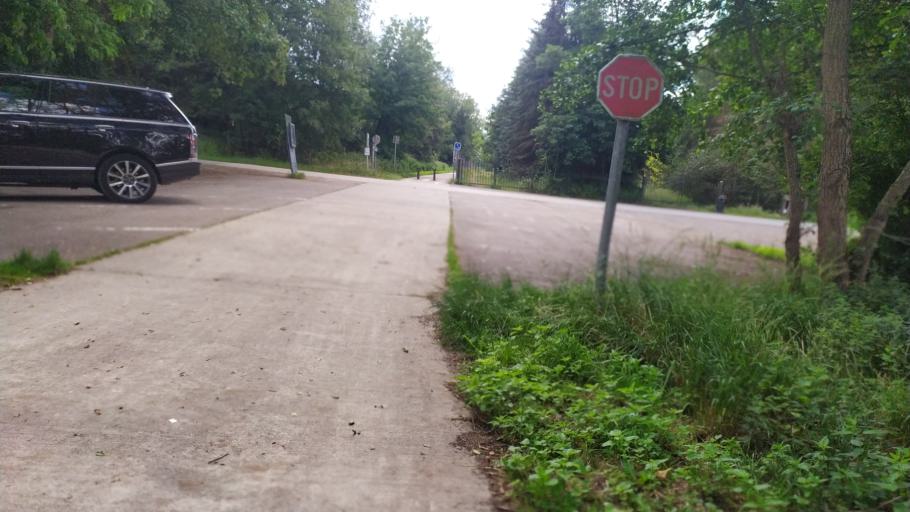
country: BE
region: Wallonia
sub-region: Province du Luxembourg
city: Wellin
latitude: 50.1610
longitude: 5.1143
